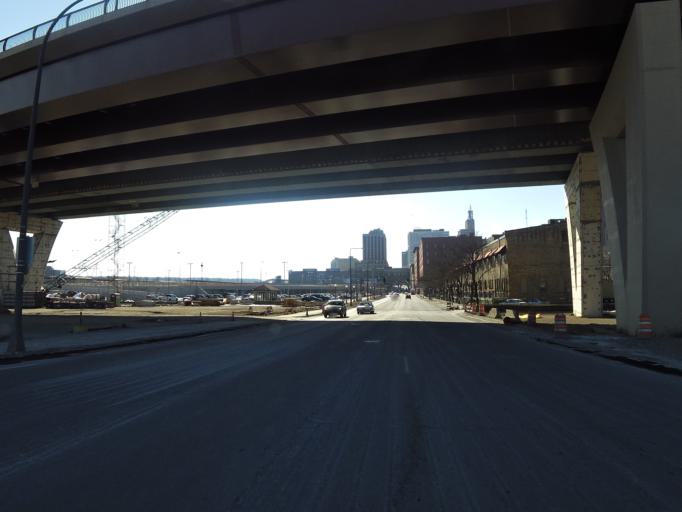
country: US
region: Minnesota
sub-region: Ramsey County
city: Saint Paul
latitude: 44.9502
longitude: -93.0804
